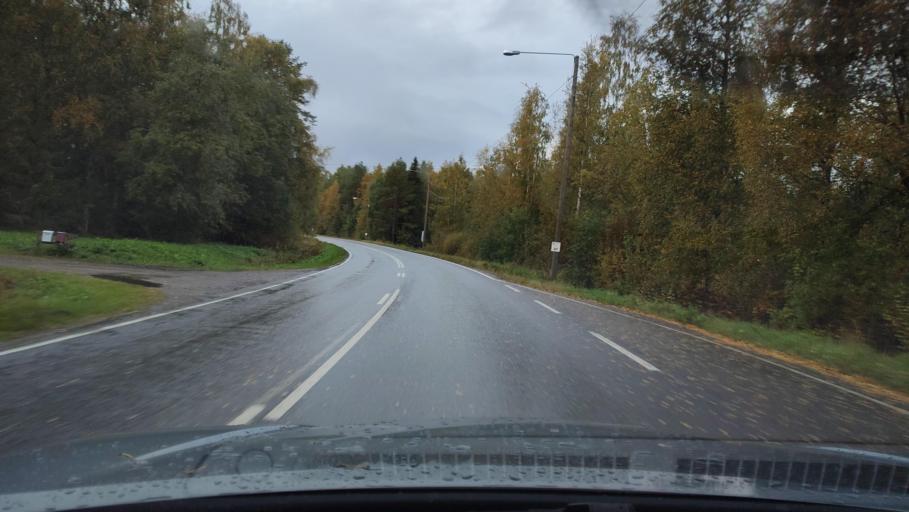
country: FI
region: Southern Ostrobothnia
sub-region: Suupohja
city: Karijoki
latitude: 62.2405
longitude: 21.6005
